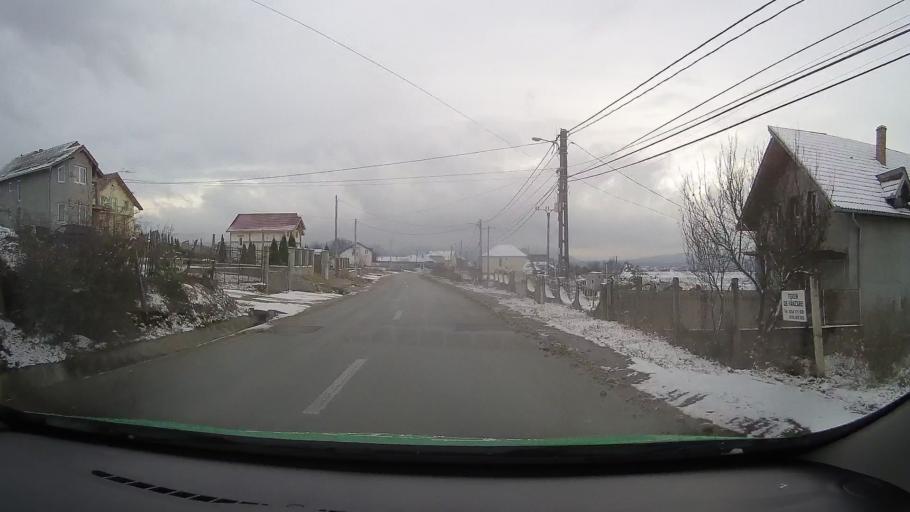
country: RO
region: Hunedoara
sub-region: Oras Hateg
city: Hateg
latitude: 45.6209
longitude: 22.9396
